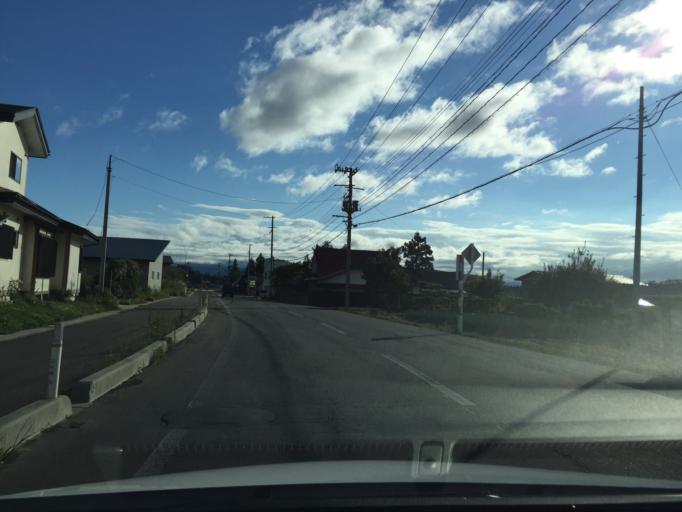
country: JP
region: Yamagata
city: Takahata
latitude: 37.9479
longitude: 140.1768
